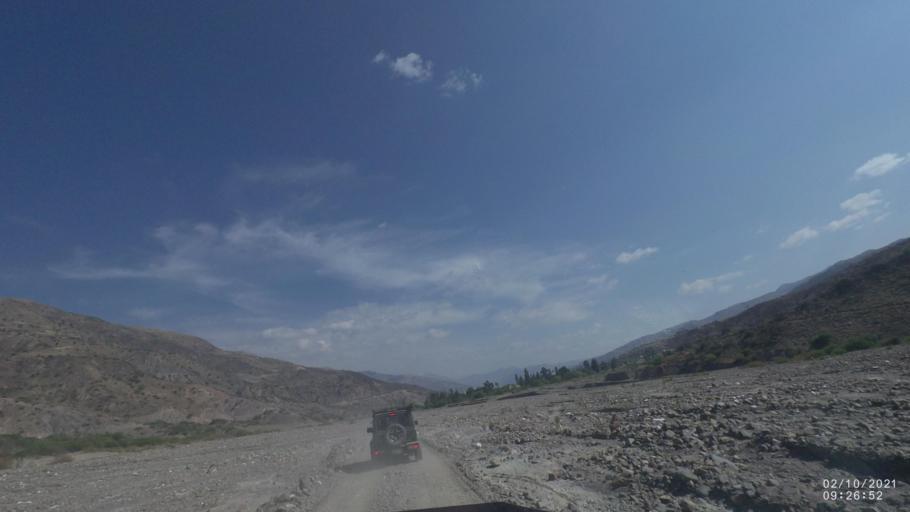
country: BO
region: Cochabamba
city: Irpa Irpa
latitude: -17.8574
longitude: -66.3140
